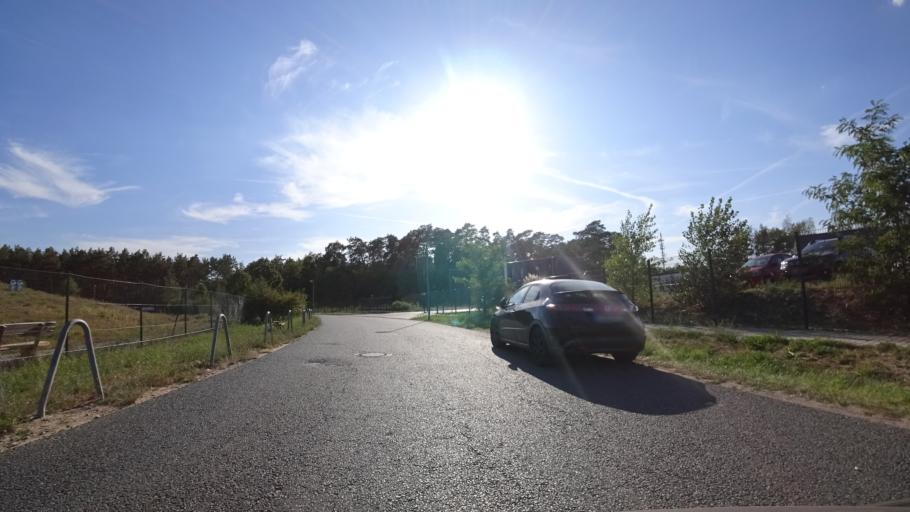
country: DE
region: Brandenburg
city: Stahnsdorf
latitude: 52.4021
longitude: 13.1933
